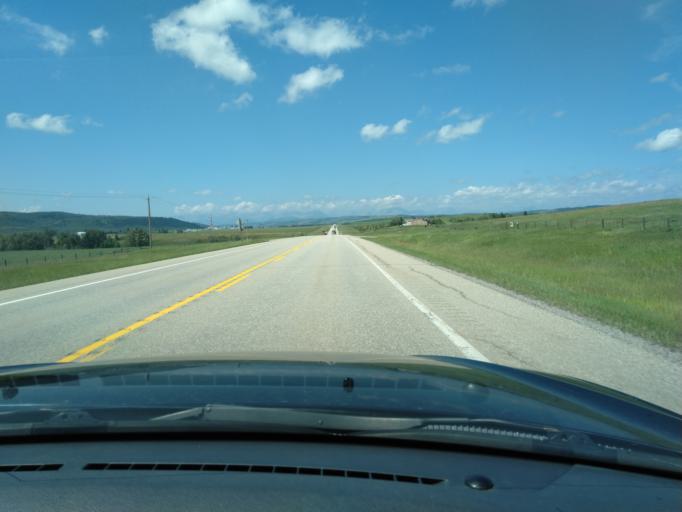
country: CA
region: Alberta
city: Cochrane
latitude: 51.2252
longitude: -114.6220
